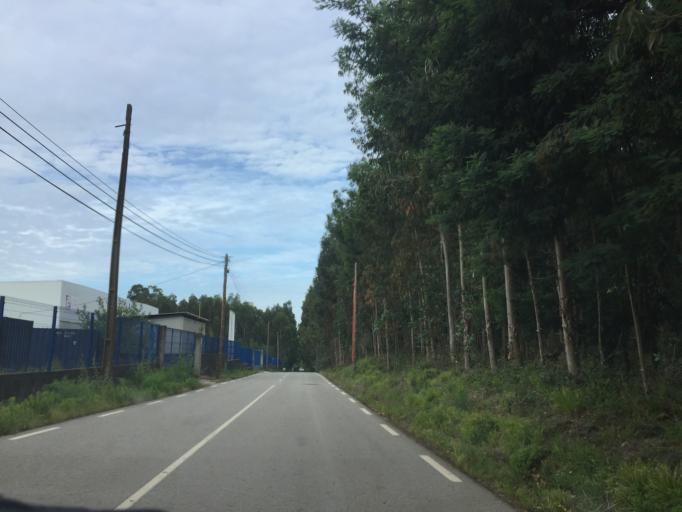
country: PT
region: Aveiro
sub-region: Agueda
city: Aguada de Cima
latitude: 40.4980
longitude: -8.3823
